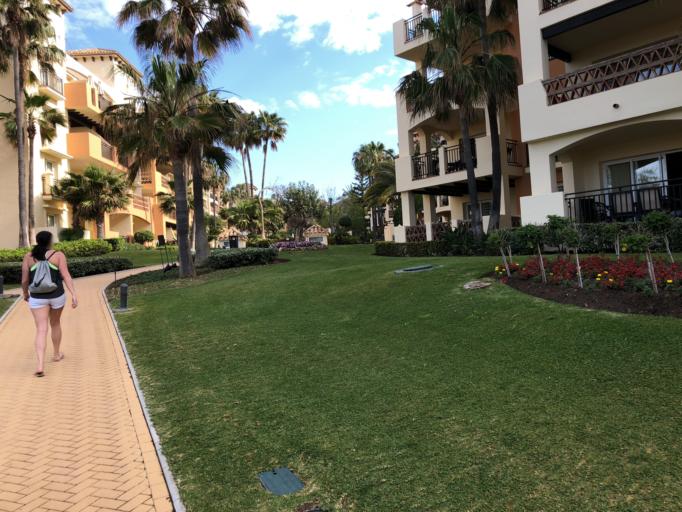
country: ES
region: Andalusia
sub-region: Provincia de Malaga
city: Ojen
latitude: 36.4896
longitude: -4.7712
